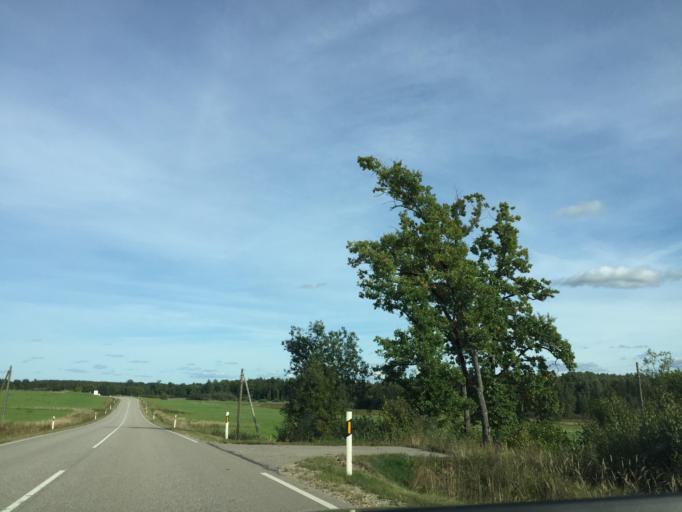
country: LV
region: Kandava
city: Kandava
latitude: 56.9394
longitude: 22.6934
